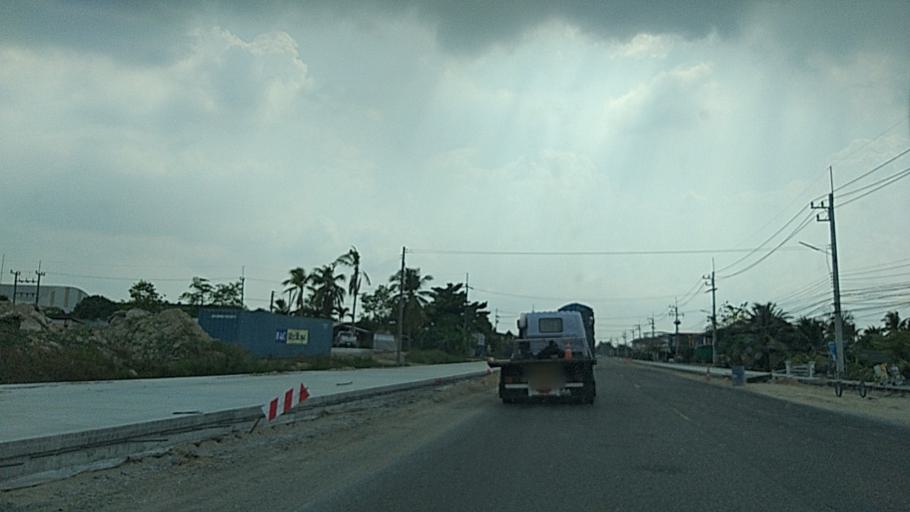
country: TH
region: Chon Buri
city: Ban Bueng
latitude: 13.3098
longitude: 101.1830
